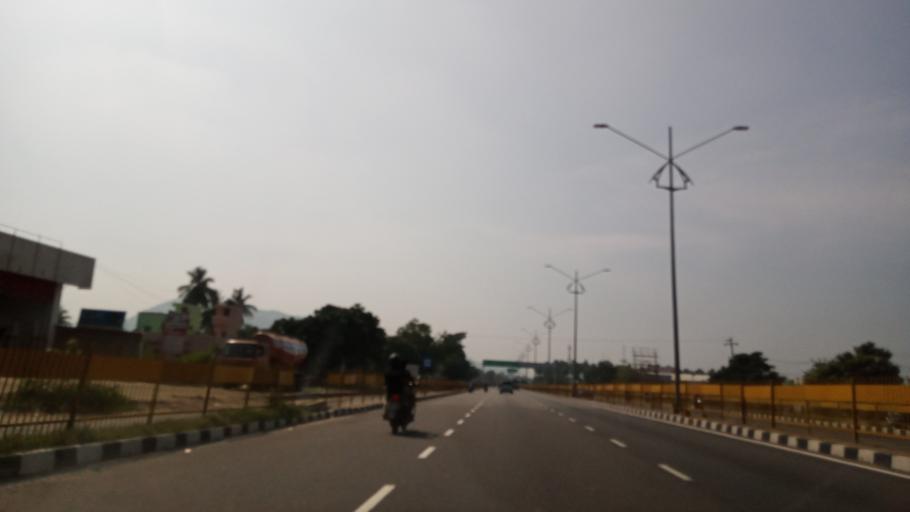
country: IN
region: Tamil Nadu
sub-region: Vellore
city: Katpadi
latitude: 12.9439
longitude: 79.1955
